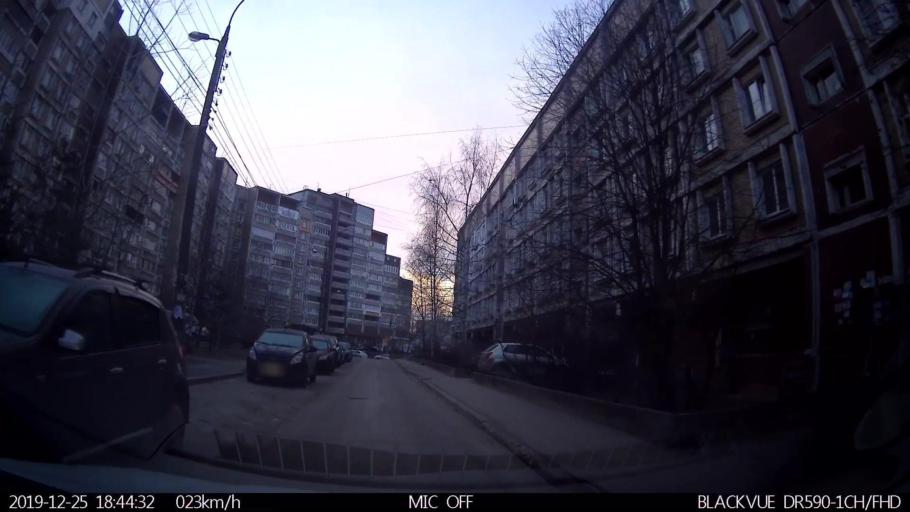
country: RU
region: Nizjnij Novgorod
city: Nizhniy Novgorod
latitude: 56.3486
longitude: 43.9229
